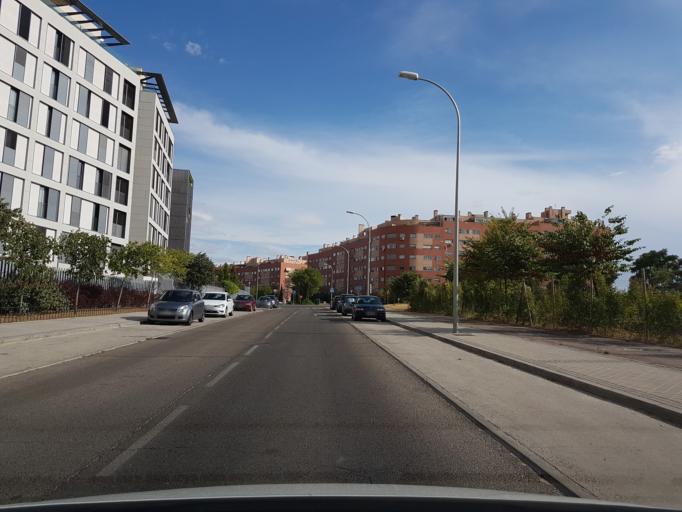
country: ES
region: Madrid
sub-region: Provincia de Madrid
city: Pinar de Chamartin
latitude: 40.4882
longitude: -3.6589
